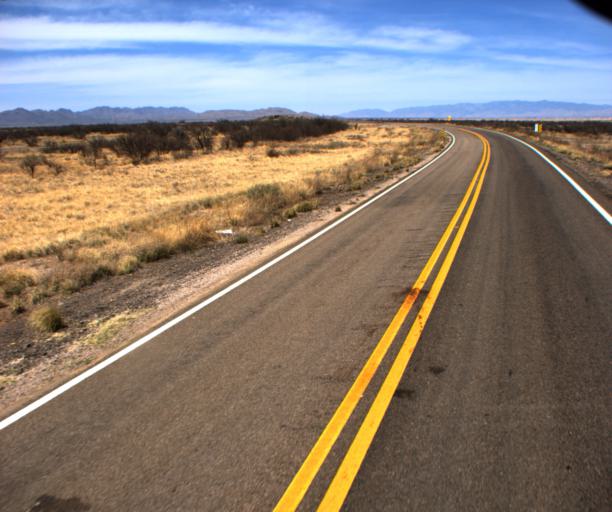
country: US
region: Arizona
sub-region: Cochise County
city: Willcox
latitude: 32.1275
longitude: -109.9084
